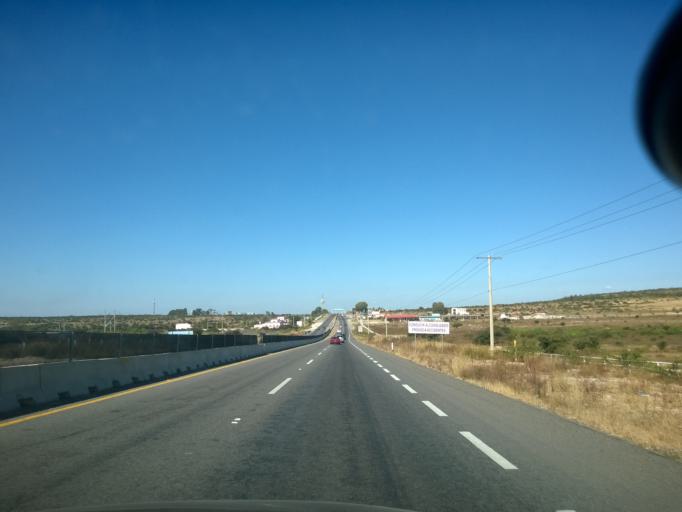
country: MX
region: Jalisco
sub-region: Lagos de Moreno
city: Geovillas Laureles del Campanario
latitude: 21.2836
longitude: -101.8416
